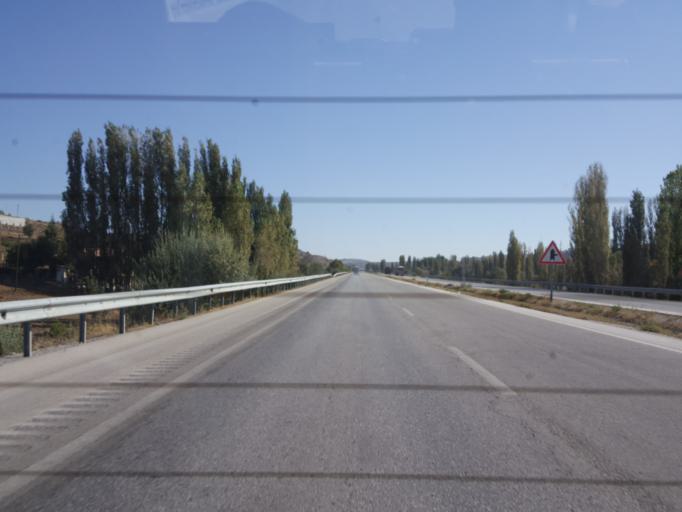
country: TR
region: Corum
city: Bogazkale
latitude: 40.2515
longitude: 34.6061
